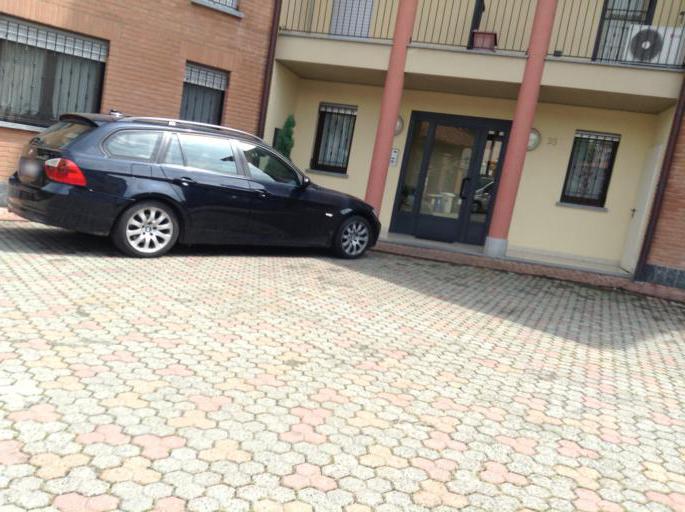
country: IT
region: Piedmont
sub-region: Provincia di Torino
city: Carignano
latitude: 44.9044
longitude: 7.6757
